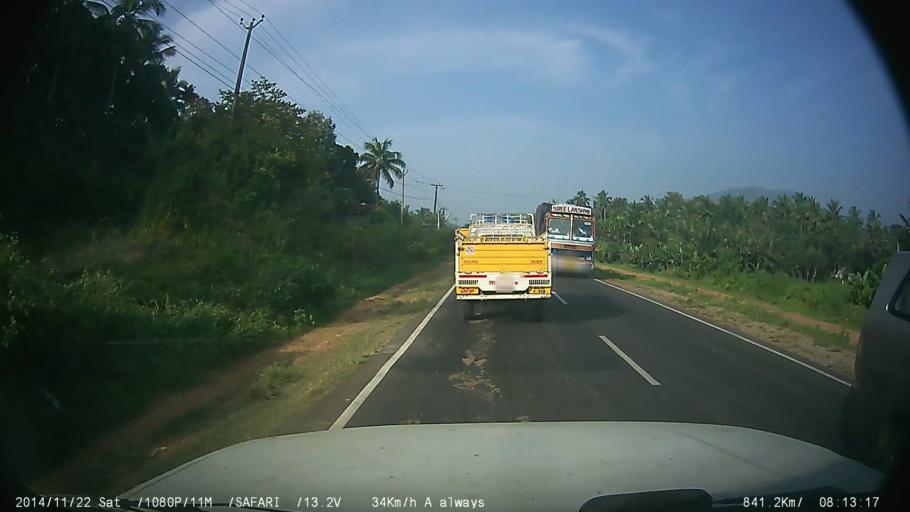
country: IN
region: Kerala
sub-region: Thrissur District
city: Chelakara
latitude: 10.5813
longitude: 76.4258
